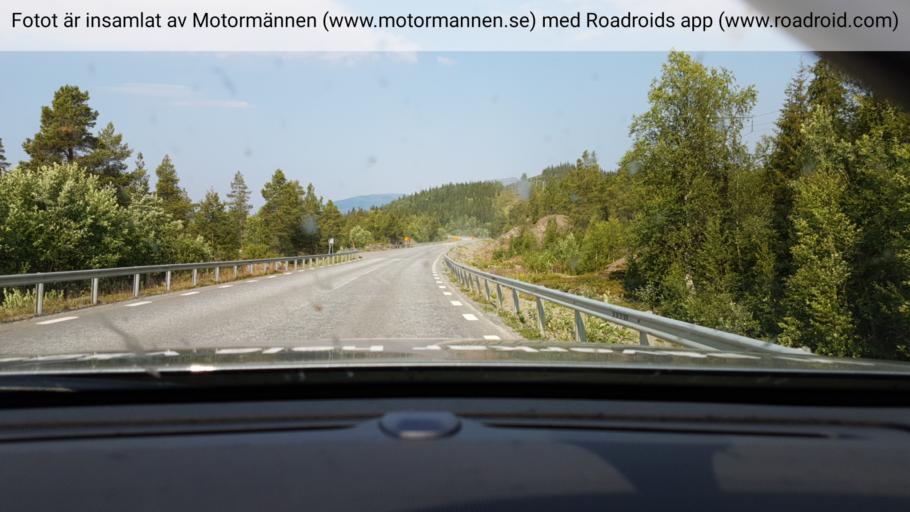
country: SE
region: Vaesterbotten
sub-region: Vilhelmina Kommun
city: Sjoberg
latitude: 65.4834
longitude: 15.8429
